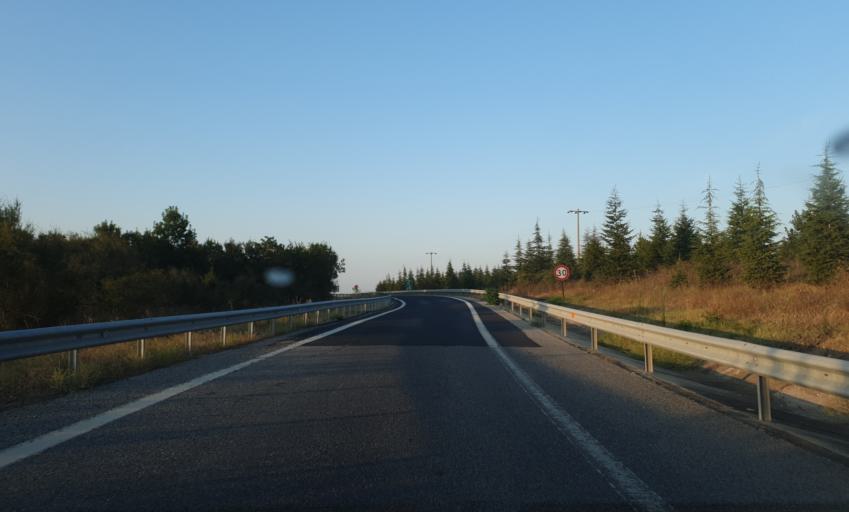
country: TR
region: Kirklareli
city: Luleburgaz
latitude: 41.4390
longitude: 27.3864
